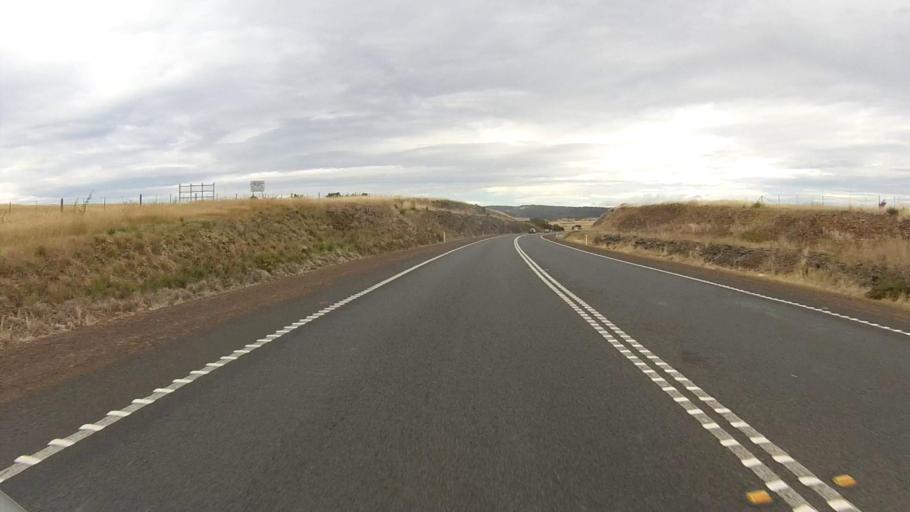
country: AU
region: Tasmania
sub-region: Brighton
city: Bridgewater
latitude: -42.3249
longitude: 147.3438
